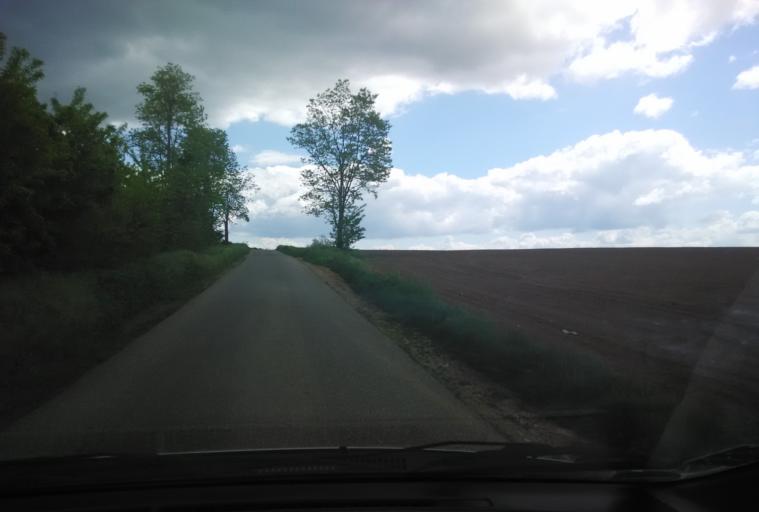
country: SK
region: Nitriansky
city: Levice
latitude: 48.2027
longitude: 18.6356
